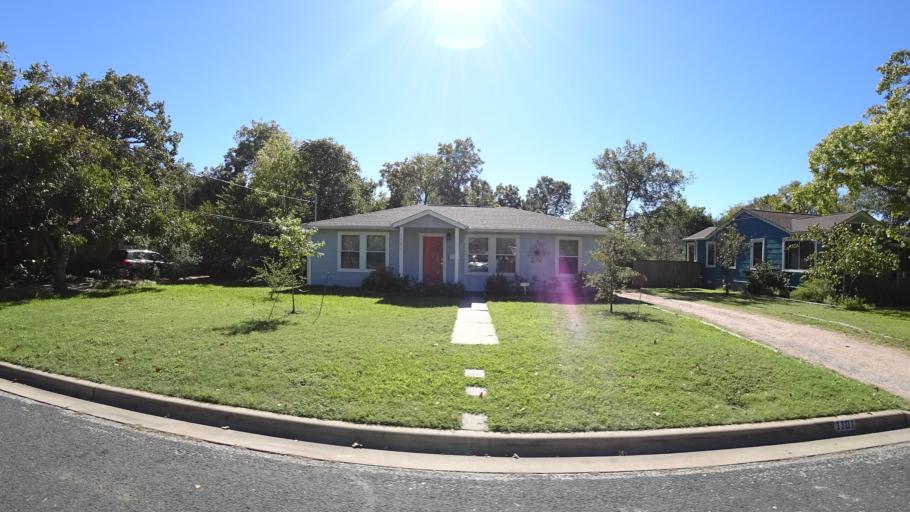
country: US
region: Texas
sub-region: Travis County
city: Austin
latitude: 30.3365
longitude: -97.7242
